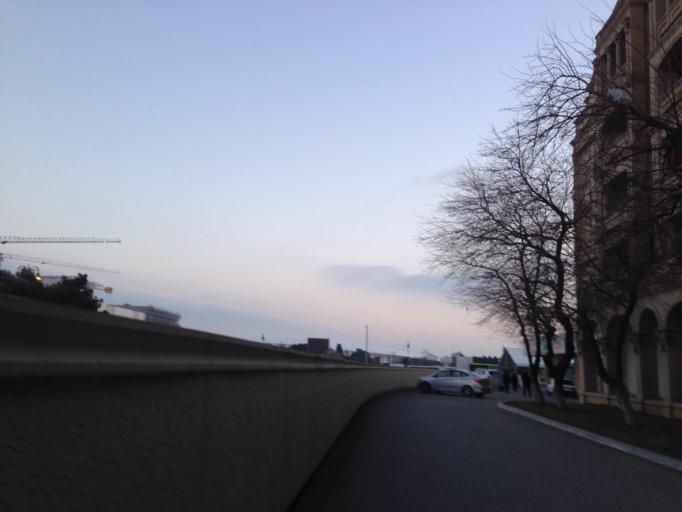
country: AZ
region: Baki
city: Baku
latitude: 40.4015
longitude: 49.8501
